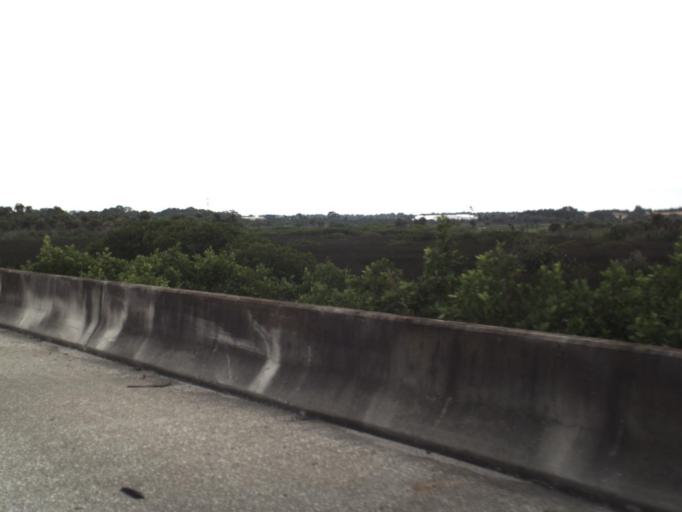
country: US
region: Florida
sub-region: Manatee County
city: Ellenton
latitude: 27.5061
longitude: -82.4913
